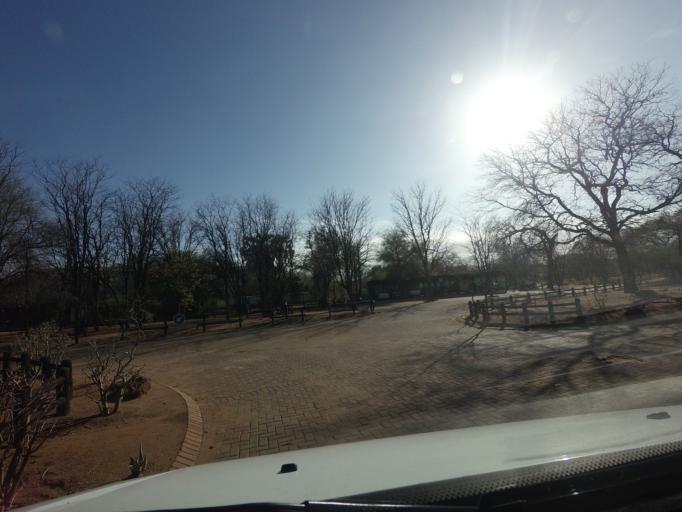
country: ZA
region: Limpopo
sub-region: Mopani District Municipality
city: Giyani
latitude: -23.1089
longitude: 31.4354
